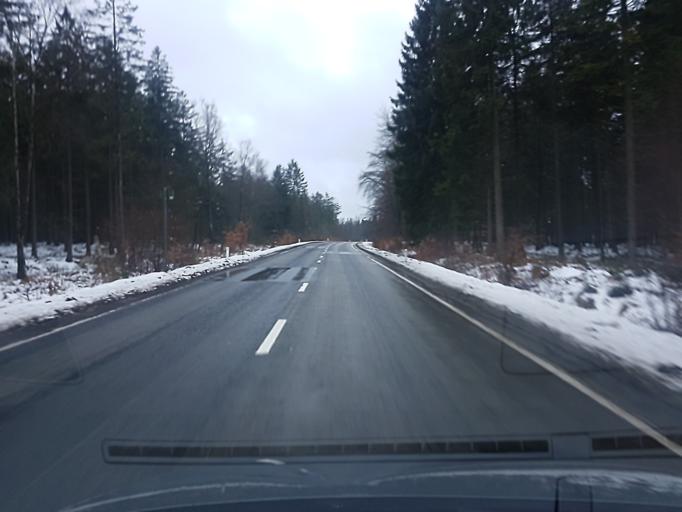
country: BE
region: Wallonia
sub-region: Province de Liege
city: Eupen
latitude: 50.5775
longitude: 6.0350
